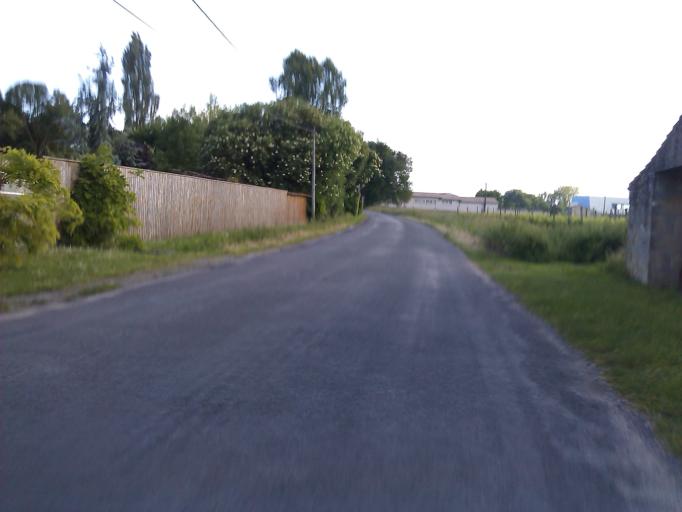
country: FR
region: Aquitaine
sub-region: Departement de la Gironde
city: Peujard
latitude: 45.0291
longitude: -0.4407
